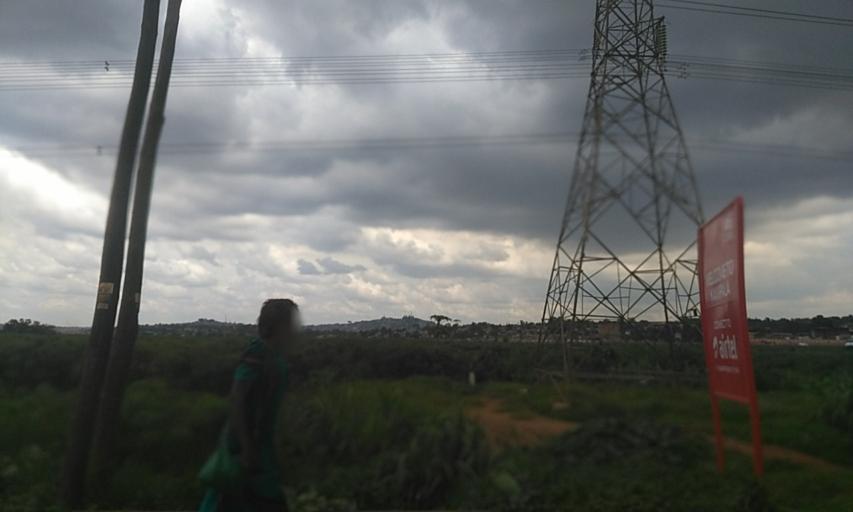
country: UG
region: Central Region
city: Kampala Central Division
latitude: 0.3143
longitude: 32.5129
